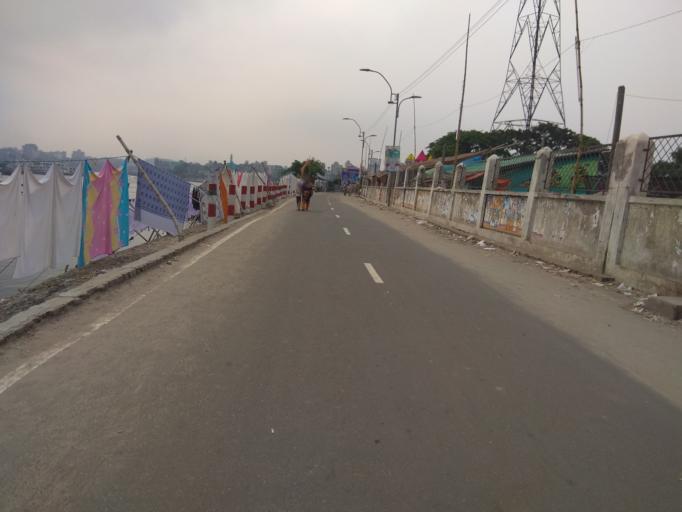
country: BD
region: Dhaka
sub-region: Dhaka
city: Dhaka
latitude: 23.7108
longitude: 90.3896
